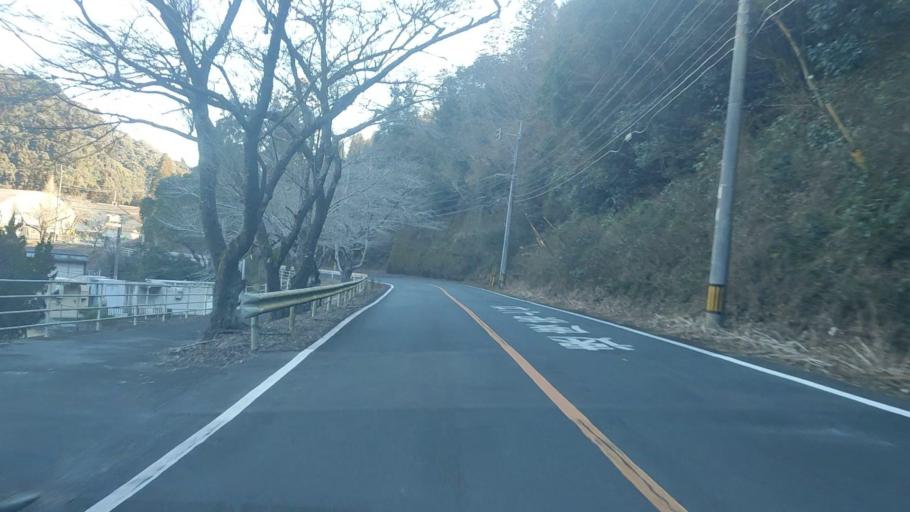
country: JP
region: Oita
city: Saiki
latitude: 32.7643
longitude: 131.7963
